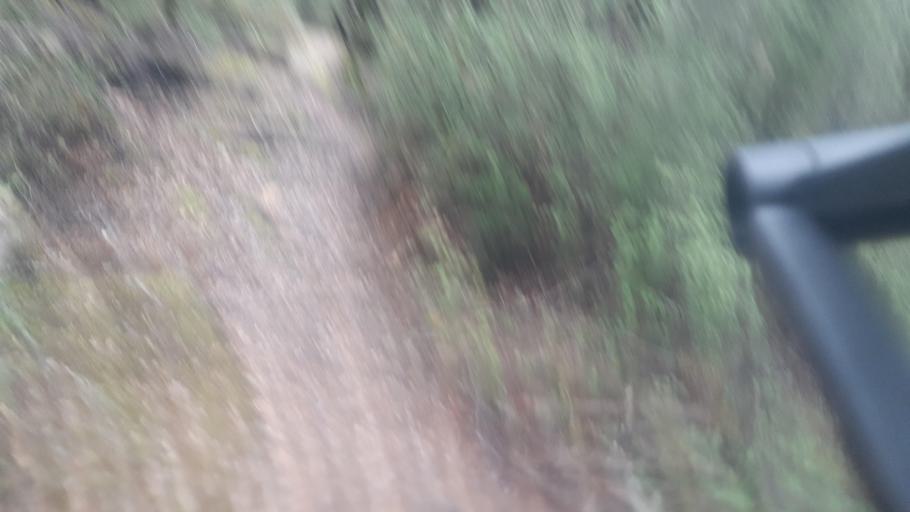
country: NZ
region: Tasman
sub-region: Tasman District
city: Wakefield
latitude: -41.7600
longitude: 172.8082
